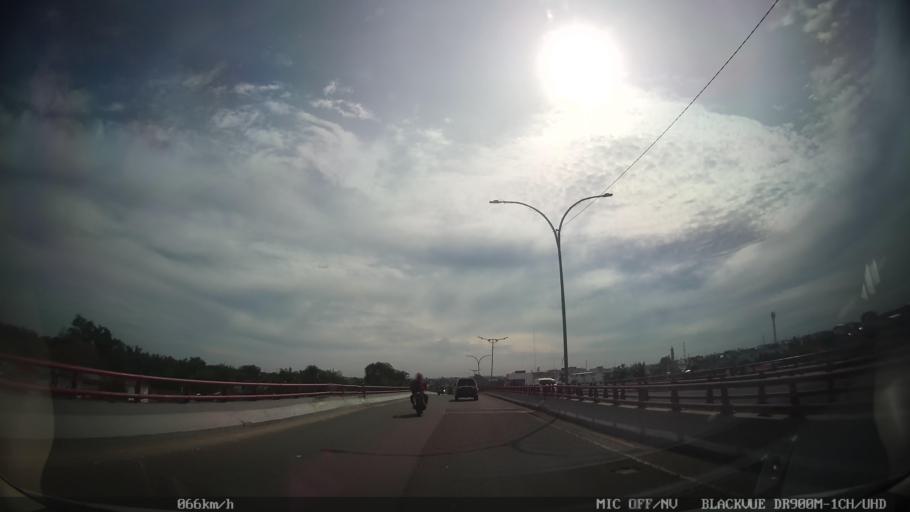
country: ID
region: North Sumatra
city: Medan
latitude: 3.6302
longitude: 98.6717
